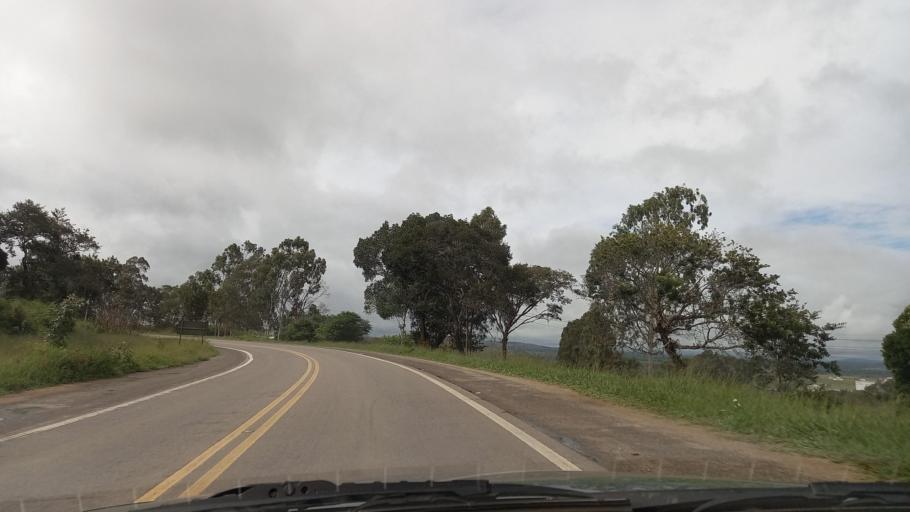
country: BR
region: Pernambuco
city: Garanhuns
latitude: -8.9108
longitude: -36.4954
